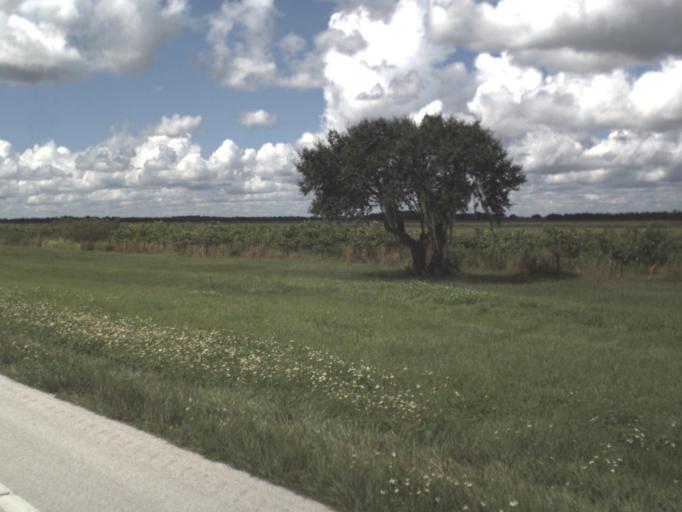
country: US
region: Florida
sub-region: DeSoto County
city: Southeast Arcadia
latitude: 27.2095
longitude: -81.7294
